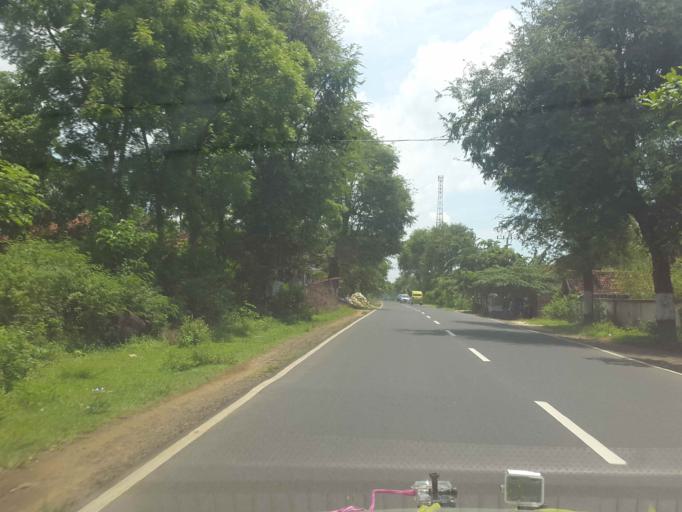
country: ID
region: East Java
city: Sumberpandan
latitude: -7.1086
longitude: 113.7081
